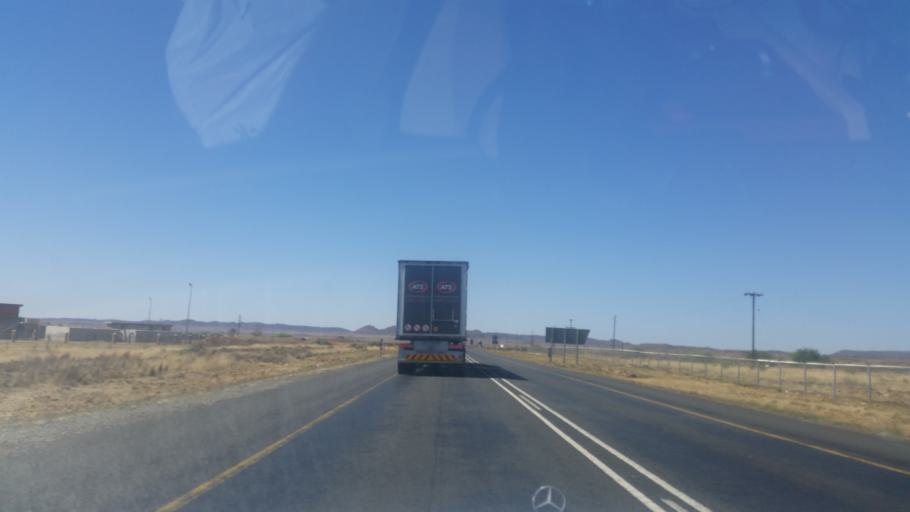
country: ZA
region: Northern Cape
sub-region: Pixley ka Seme District Municipality
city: Colesberg
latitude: -30.7059
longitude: 25.1136
